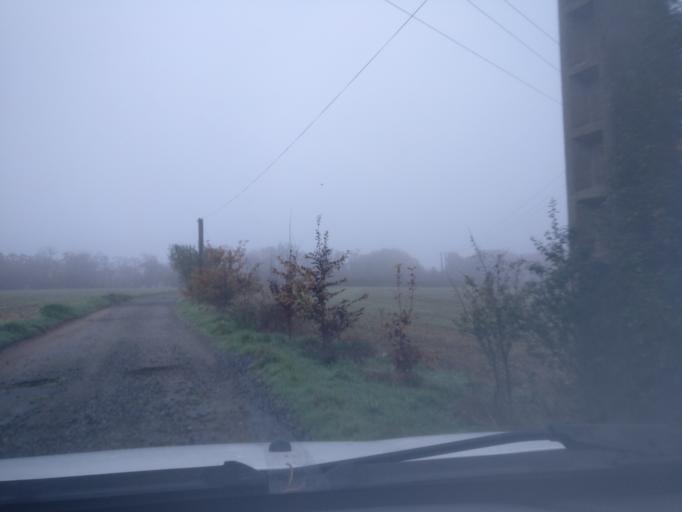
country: FR
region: Brittany
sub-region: Departement d'Ille-et-Vilaine
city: Bruz
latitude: 48.0043
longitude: -1.7634
